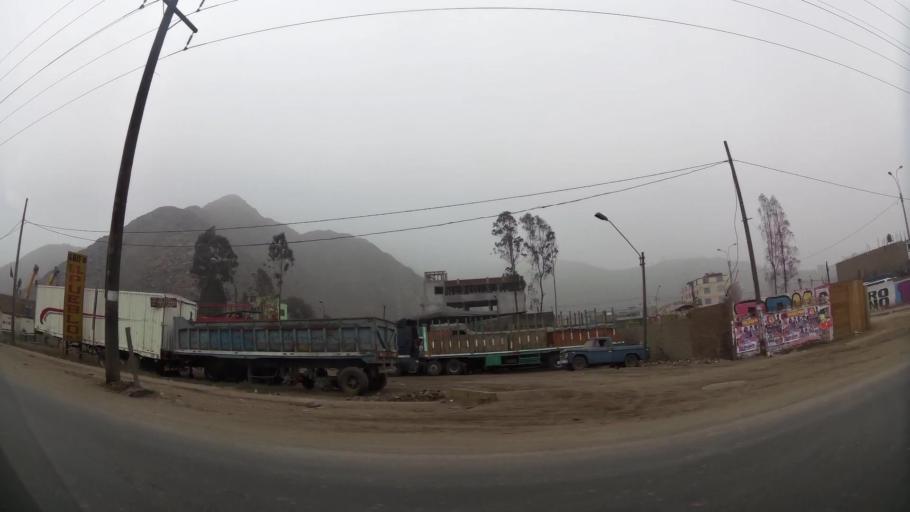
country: PE
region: Lima
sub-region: Lima
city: Santa Maria
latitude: -12.0097
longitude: -76.8679
